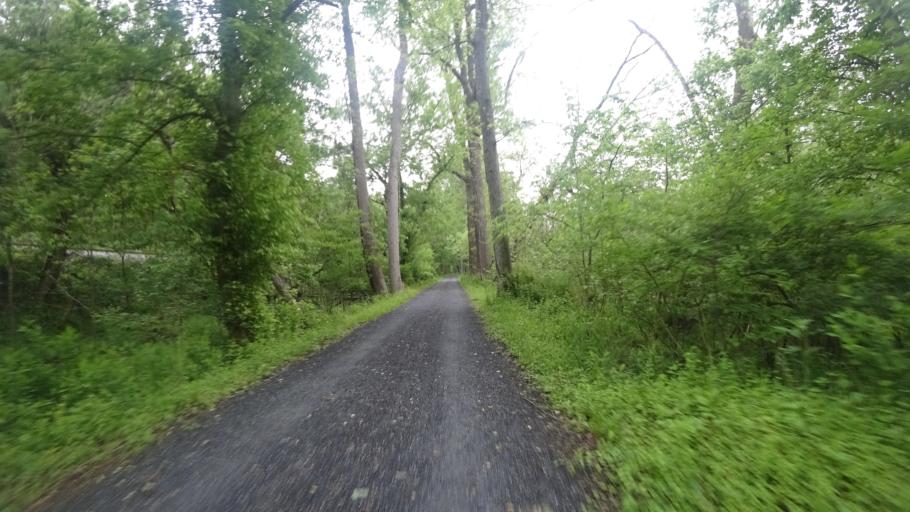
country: US
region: Maryland
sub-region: Frederick County
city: Brunswick
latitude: 39.3092
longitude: -77.5792
